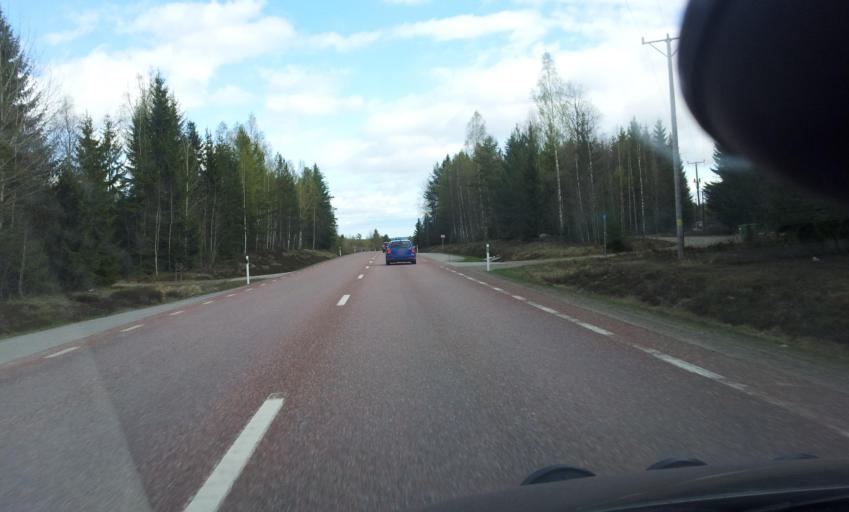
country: SE
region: Gaevleborg
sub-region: Ljusdals Kommun
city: Ljusdal
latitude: 61.7830
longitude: 16.1375
